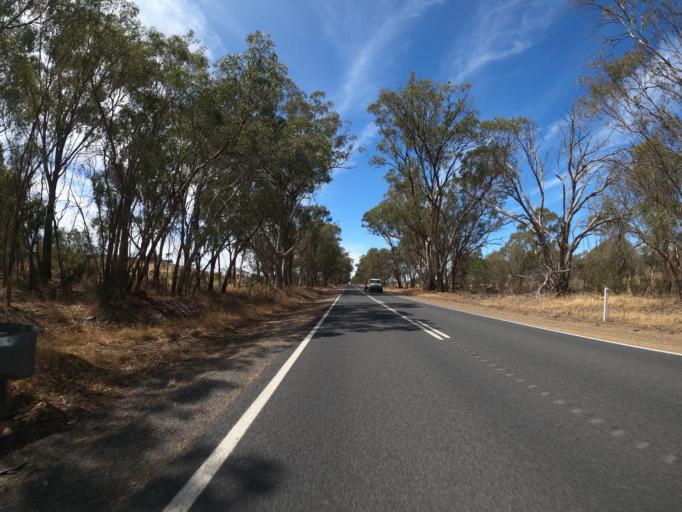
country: AU
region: Victoria
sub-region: Benalla
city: Benalla
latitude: -36.3706
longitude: 145.9723
